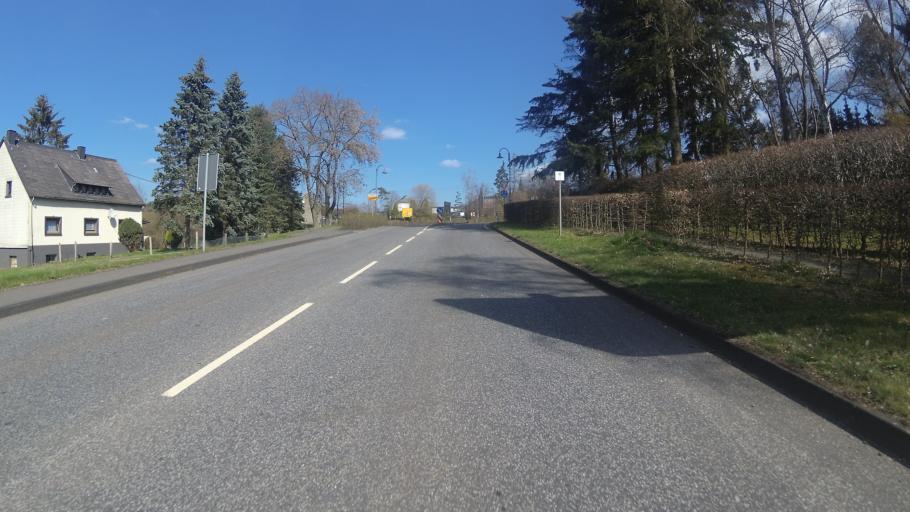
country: DE
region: Rheinland-Pfalz
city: Kelberg
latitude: 50.2847
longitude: 6.9217
